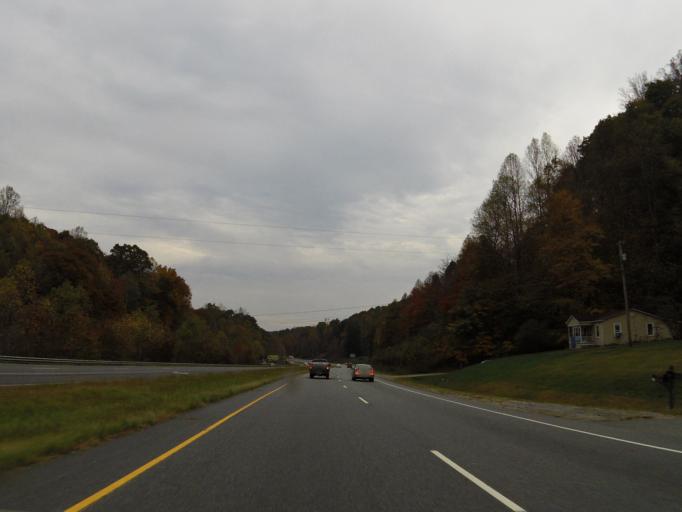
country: US
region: North Carolina
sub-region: Caldwell County
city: Lenoir
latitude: 35.9641
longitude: -81.5649
